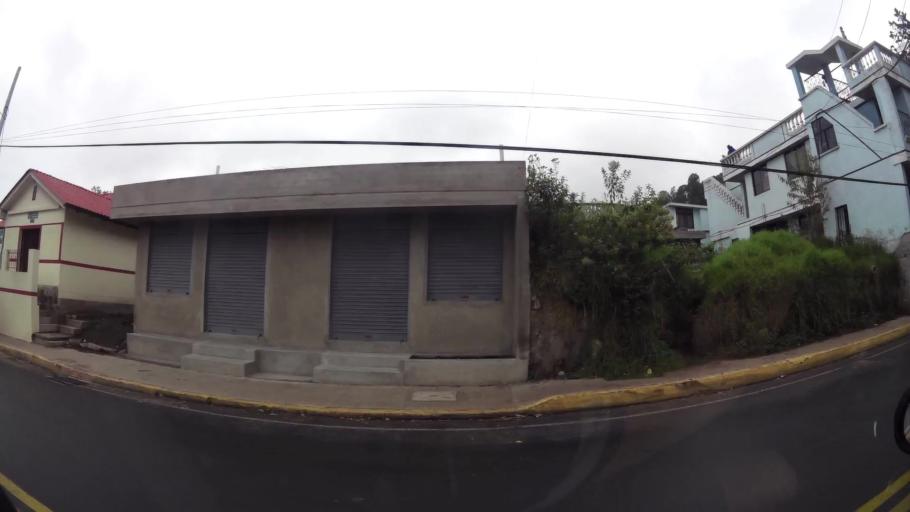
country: EC
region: Pichincha
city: Sangolqui
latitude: -0.2673
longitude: -78.4646
